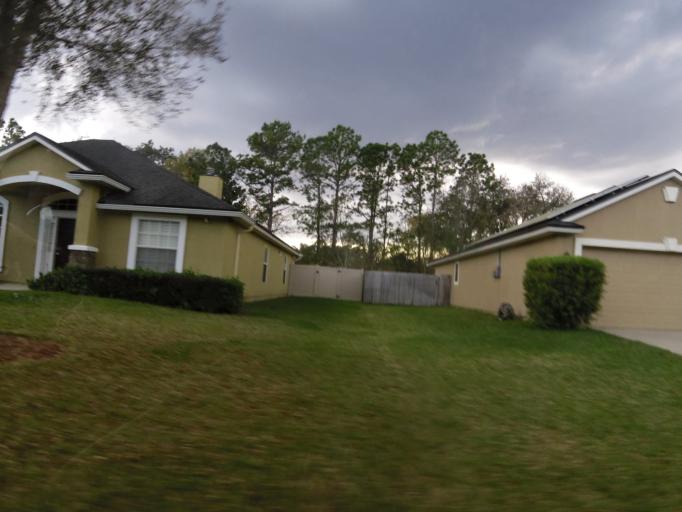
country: US
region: Florida
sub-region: Saint Johns County
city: Fruit Cove
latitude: 30.1714
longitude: -81.5776
